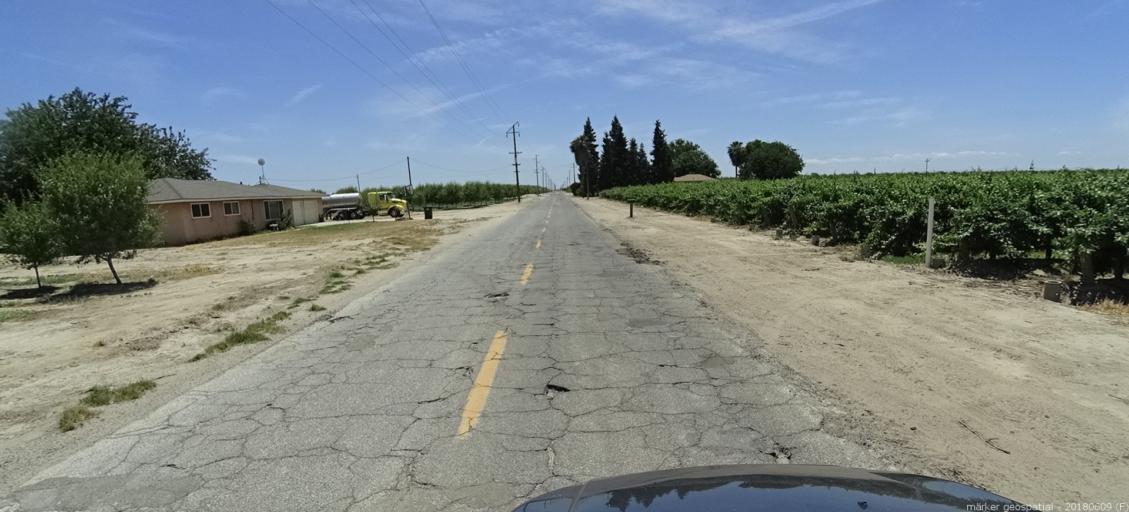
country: US
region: California
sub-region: Madera County
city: Parkwood
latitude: 36.8532
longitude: -120.1103
